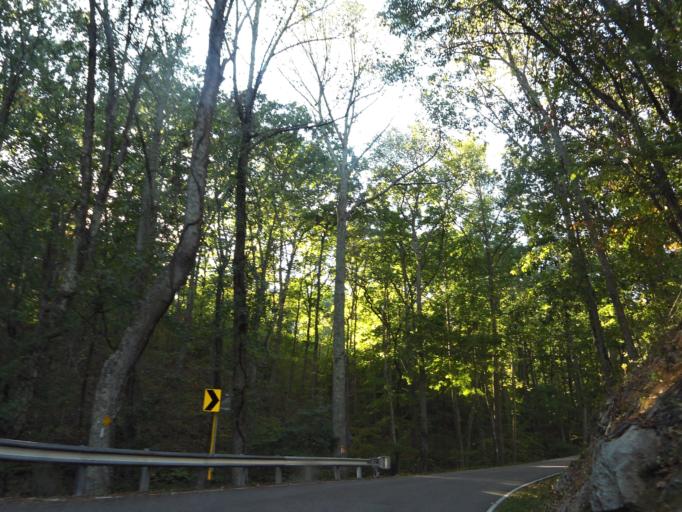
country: US
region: Tennessee
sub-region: Grainger County
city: Blaine
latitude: 36.2374
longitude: -83.6456
